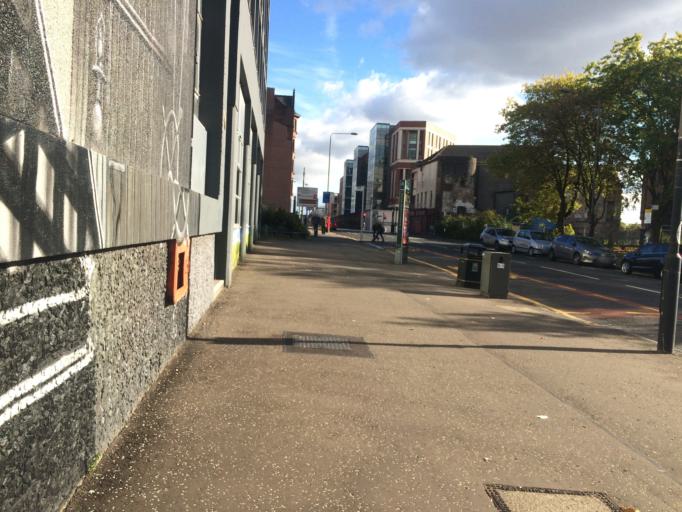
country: GB
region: Scotland
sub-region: Glasgow City
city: Glasgow
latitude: 55.8606
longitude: -4.2415
